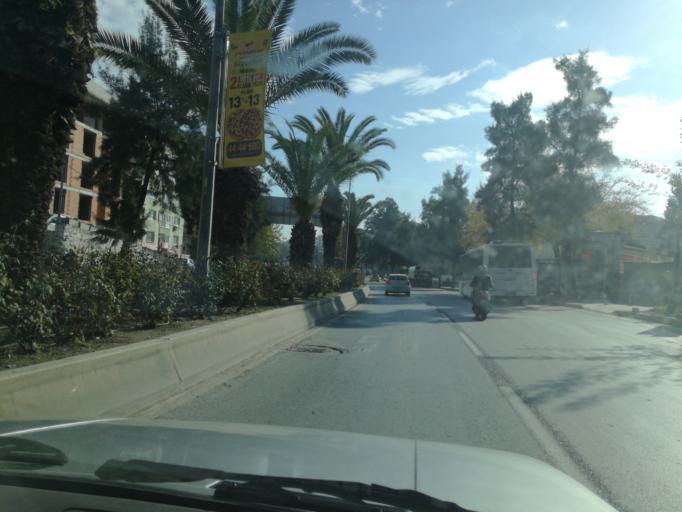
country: TR
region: Izmir
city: Izmir
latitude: 38.4044
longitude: 27.1226
